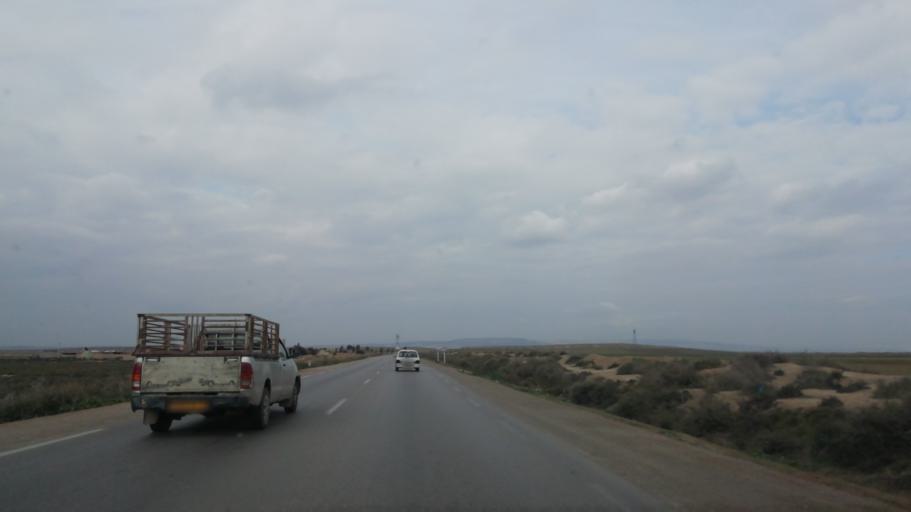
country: DZ
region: Mostaganem
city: Mostaganem
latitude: 35.7029
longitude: 0.0550
